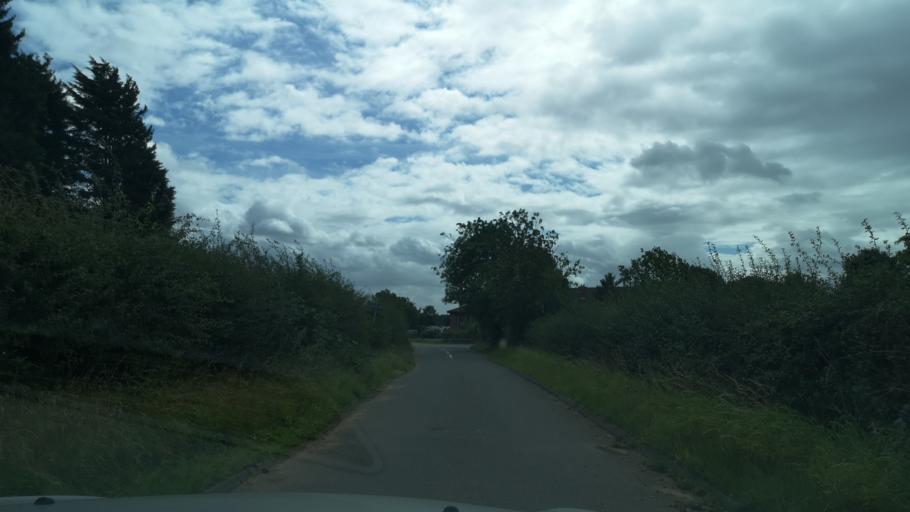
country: GB
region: England
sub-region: City and Borough of Wakefield
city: Darrington
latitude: 53.6784
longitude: -1.2582
